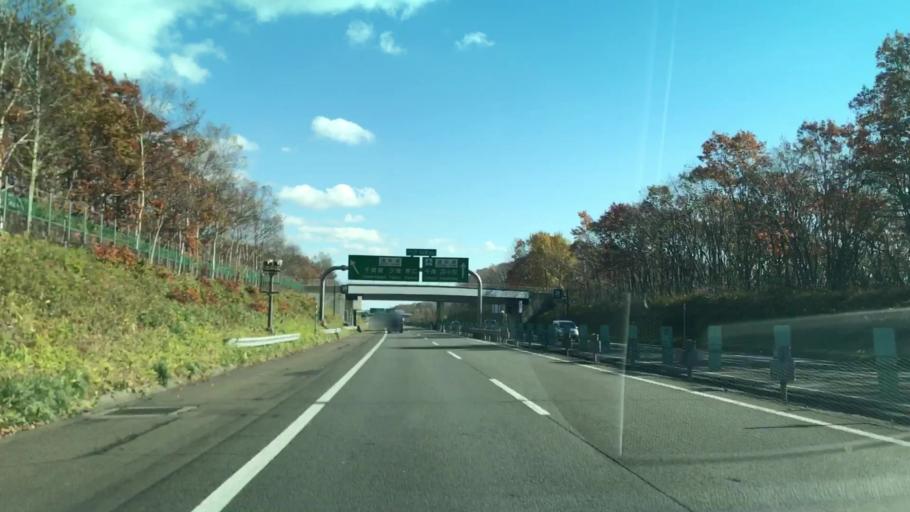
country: JP
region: Hokkaido
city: Chitose
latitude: 42.8484
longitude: 141.5759
